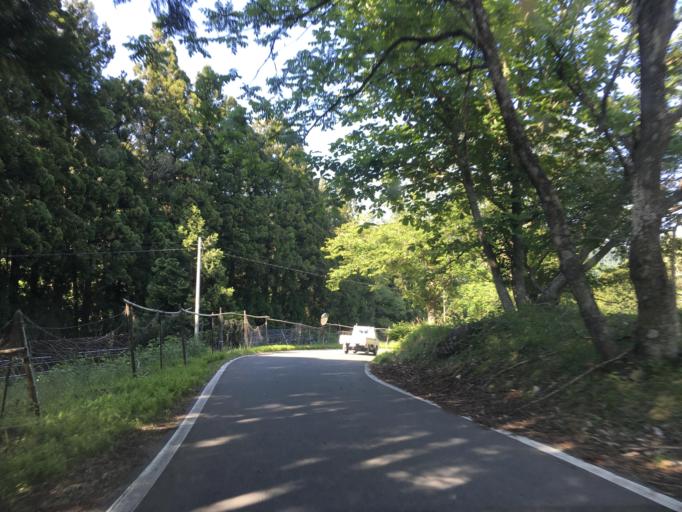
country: JP
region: Iwate
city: Kamaishi
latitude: 39.1944
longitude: 141.8183
